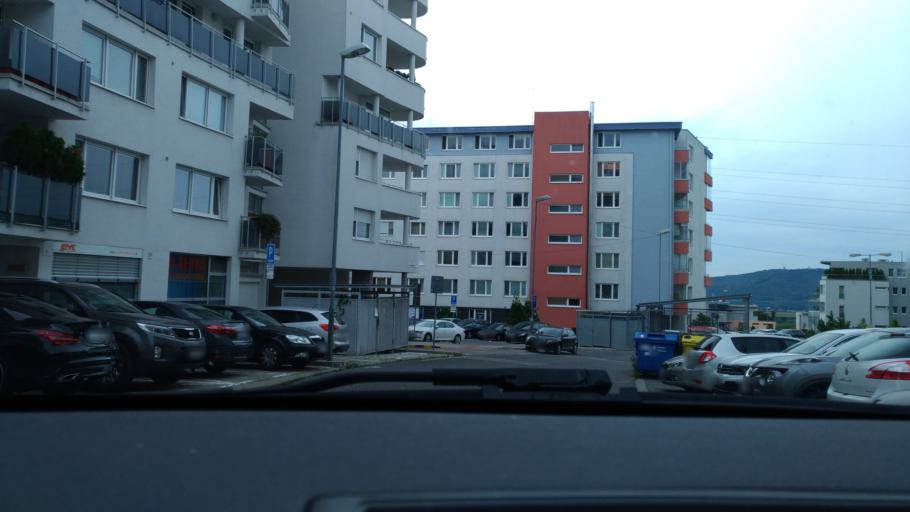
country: AT
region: Lower Austria
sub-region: Politischer Bezirk Bruck an der Leitha
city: Berg
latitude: 48.1497
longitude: 17.0504
